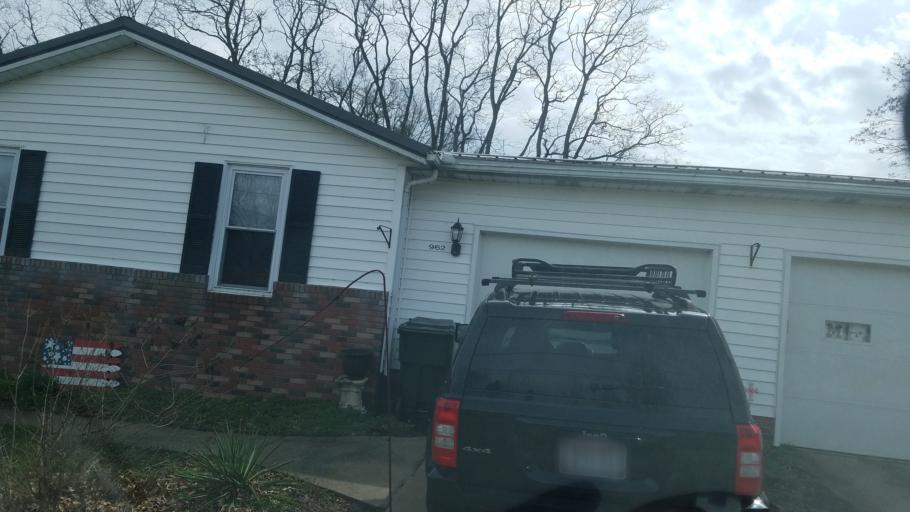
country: US
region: Ohio
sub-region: Wayne County
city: Wooster
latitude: 40.7667
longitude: -81.9585
